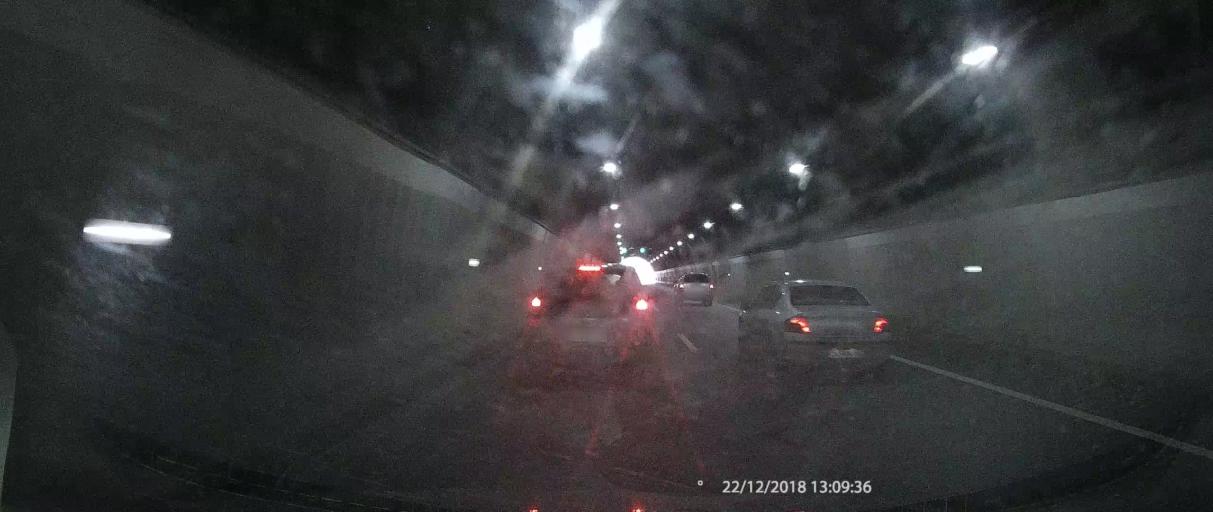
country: BG
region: Sofiya
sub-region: Obshtina Botevgrad
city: Botevgrad
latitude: 42.8573
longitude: 23.7917
